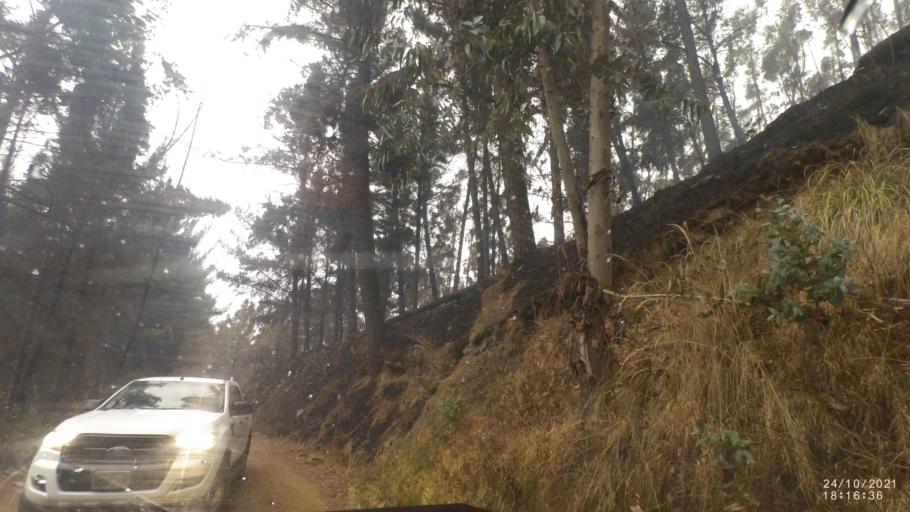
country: BO
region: Cochabamba
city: Cochabamba
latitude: -17.3315
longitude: -66.1380
